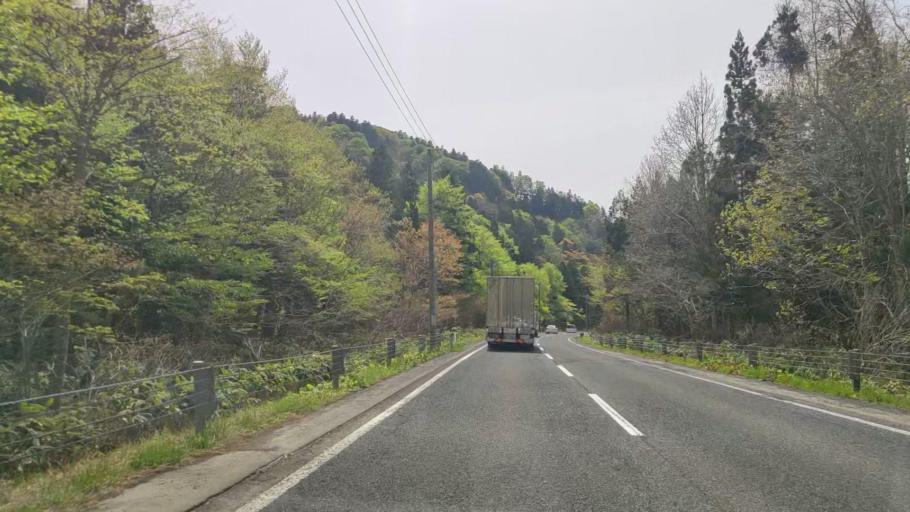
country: JP
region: Aomori
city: Aomori Shi
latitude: 40.7772
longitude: 141.0247
